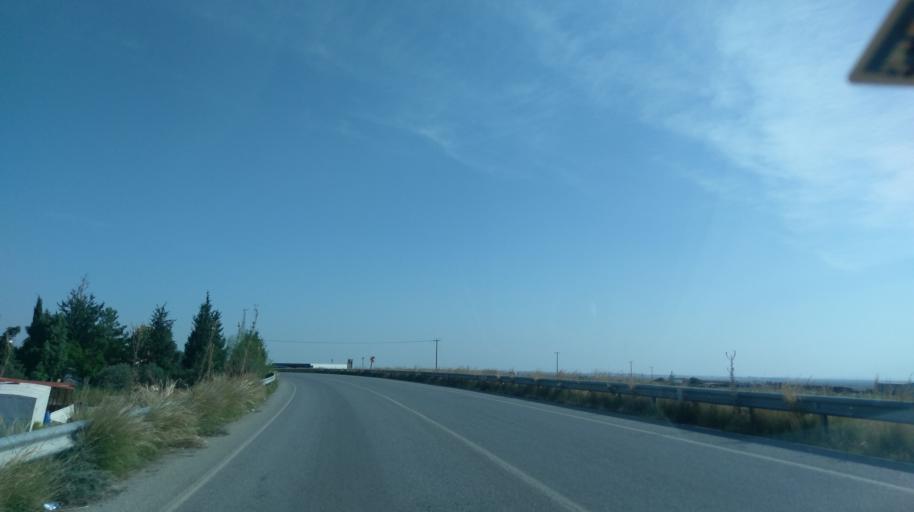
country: CY
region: Ammochostos
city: Lefkonoiko
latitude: 35.2423
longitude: 33.6006
